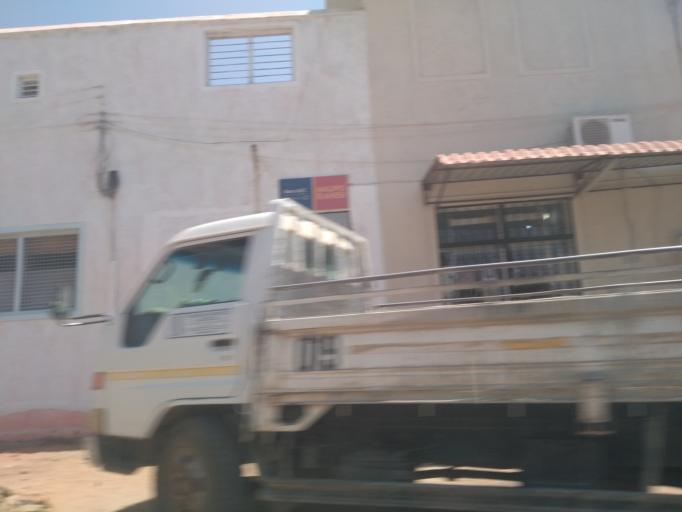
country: TZ
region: Dodoma
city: Dodoma
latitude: -6.1785
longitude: 35.7491
